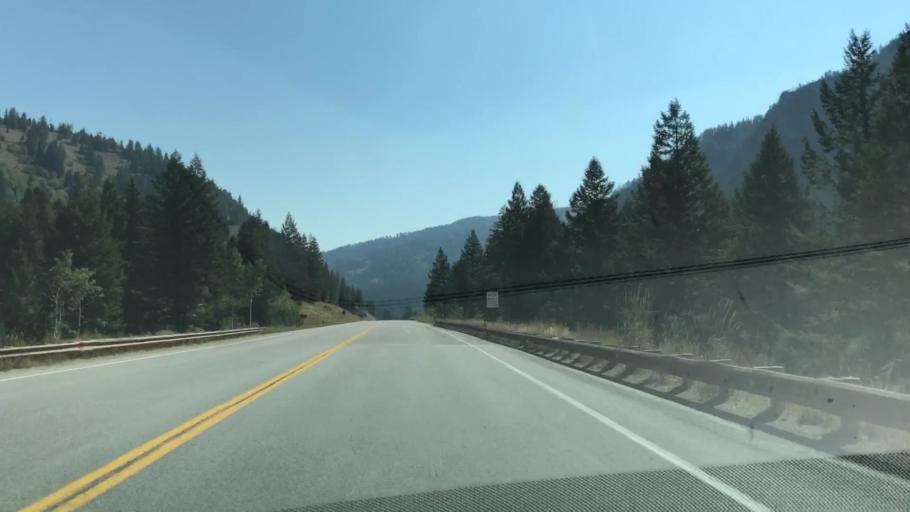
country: US
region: Wyoming
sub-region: Teton County
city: Hoback
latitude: 43.1982
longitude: -110.9016
